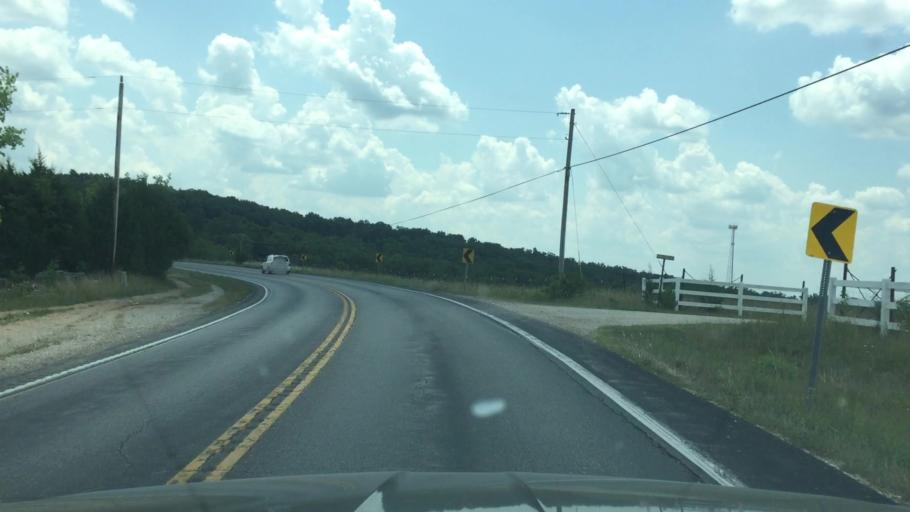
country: US
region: Missouri
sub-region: Miller County
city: Tuscumbia
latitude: 38.1013
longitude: -92.4986
